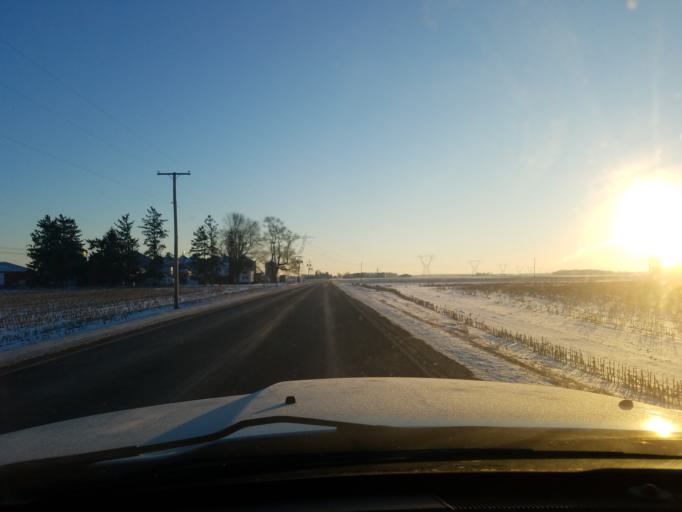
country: US
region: Indiana
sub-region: Marshall County
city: Bremen
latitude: 41.4499
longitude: -86.2353
